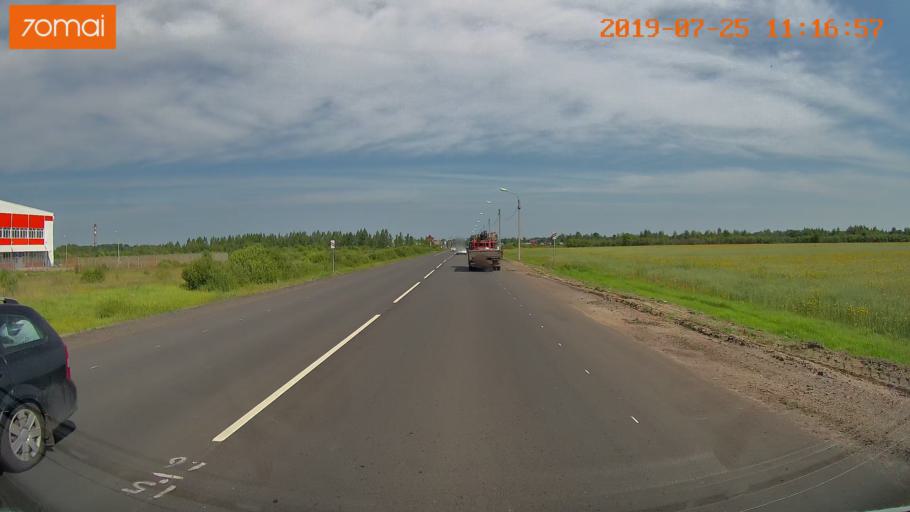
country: RU
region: Ivanovo
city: Privolzhsk
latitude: 57.3631
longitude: 41.2682
